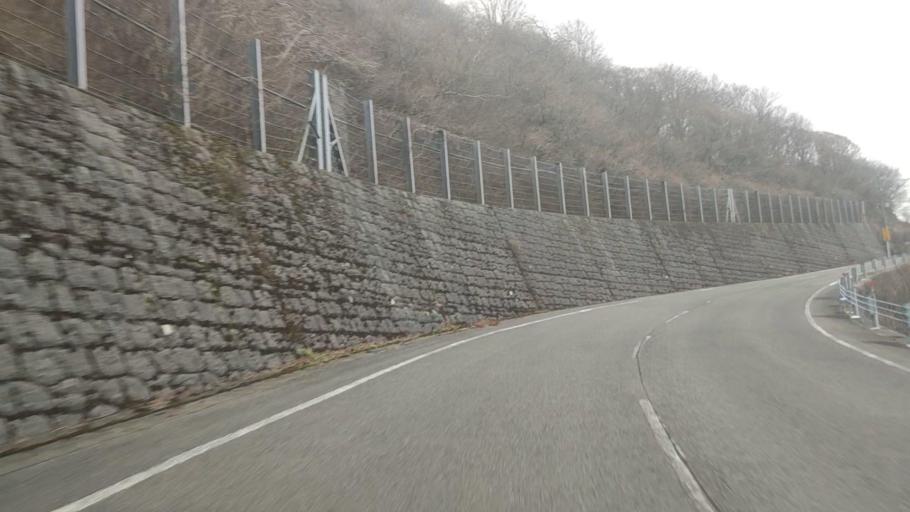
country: JP
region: Nagasaki
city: Shimabara
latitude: 32.7564
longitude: 130.2759
